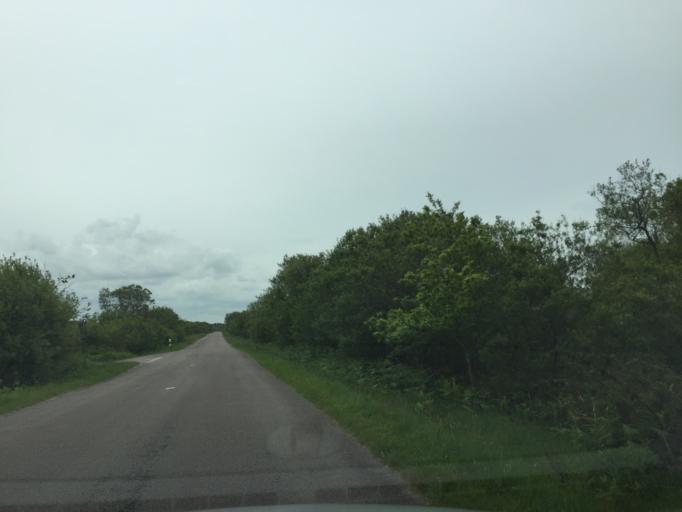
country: FR
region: Brittany
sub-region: Departement des Cotes-d'Armor
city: Saint-Cast-le-Guildo
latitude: 48.6754
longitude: -2.3183
